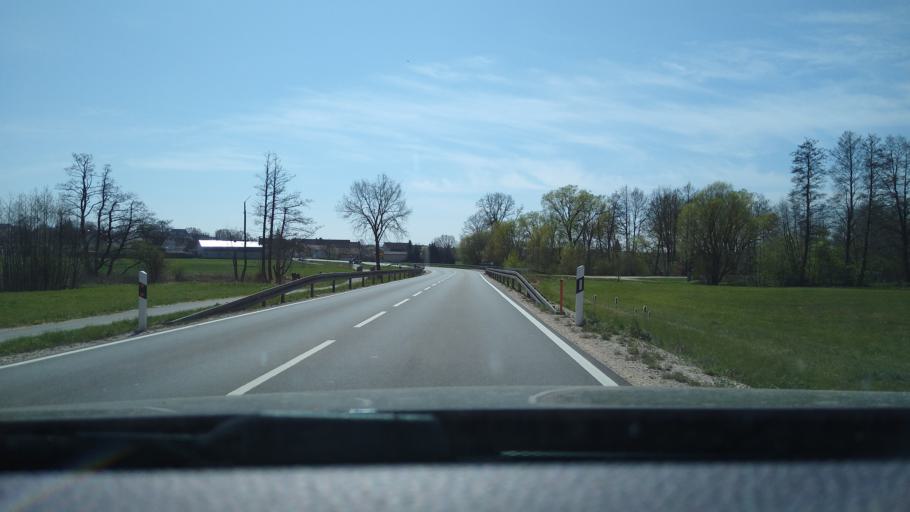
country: DE
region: Bavaria
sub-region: Regierungsbezirk Mittelfranken
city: Muhr am See
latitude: 49.1631
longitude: 10.7156
